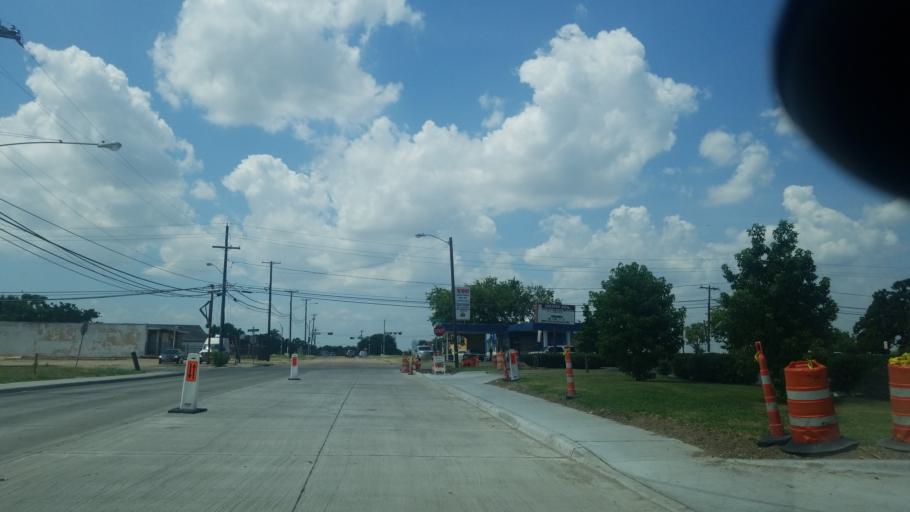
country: US
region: Texas
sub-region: Dallas County
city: Dallas
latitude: 32.7147
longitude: -96.7760
